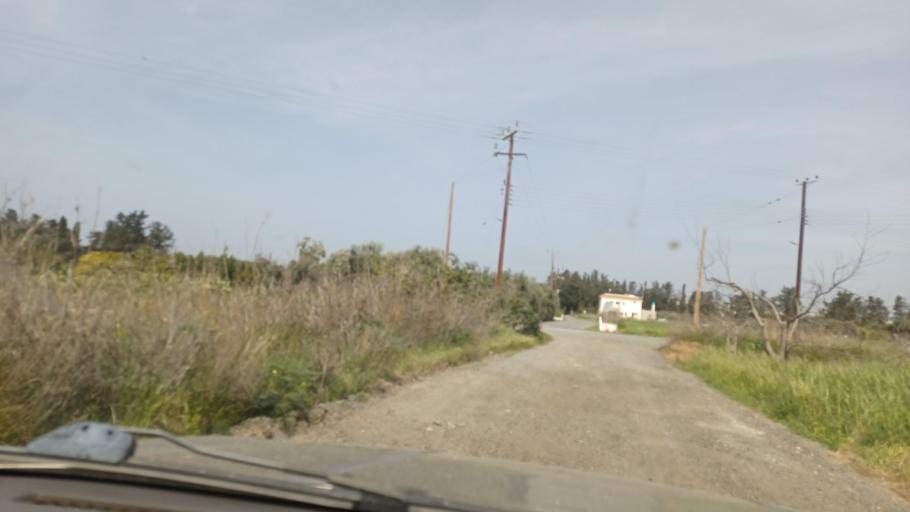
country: CY
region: Pafos
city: Paphos
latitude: 34.7448
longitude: 32.4619
